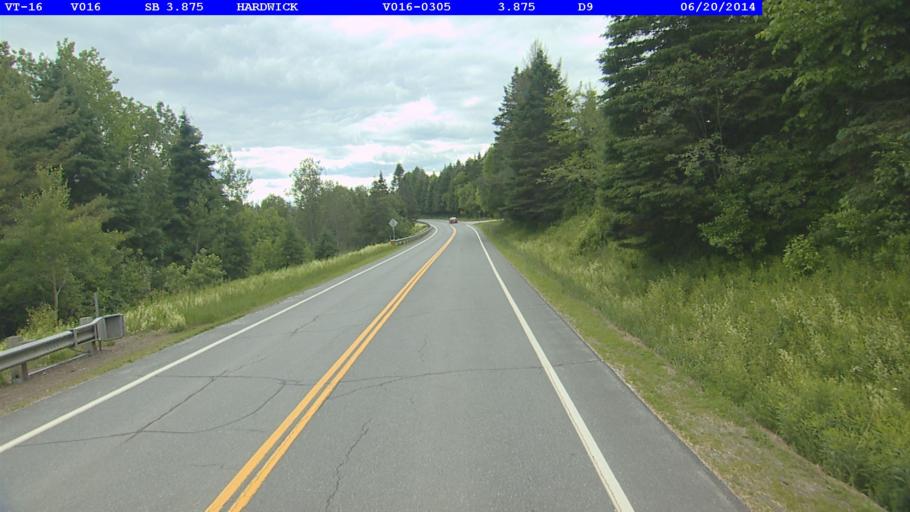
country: US
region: Vermont
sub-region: Caledonia County
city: Hardwick
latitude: 44.5375
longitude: -72.2727
